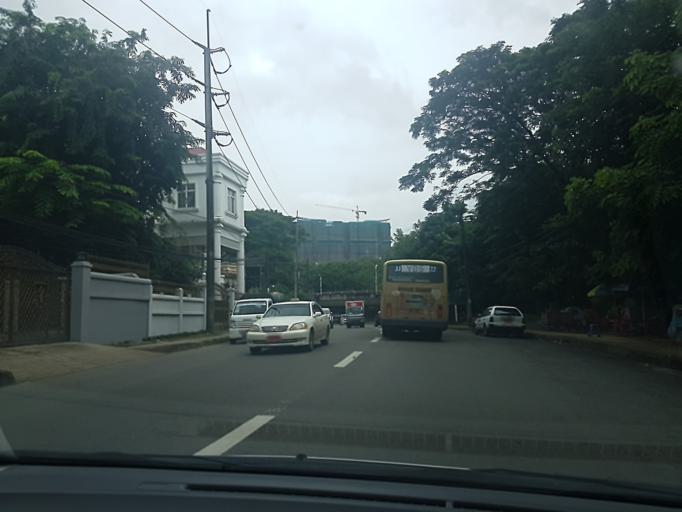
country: MM
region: Yangon
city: Yangon
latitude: 16.8215
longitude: 96.1260
